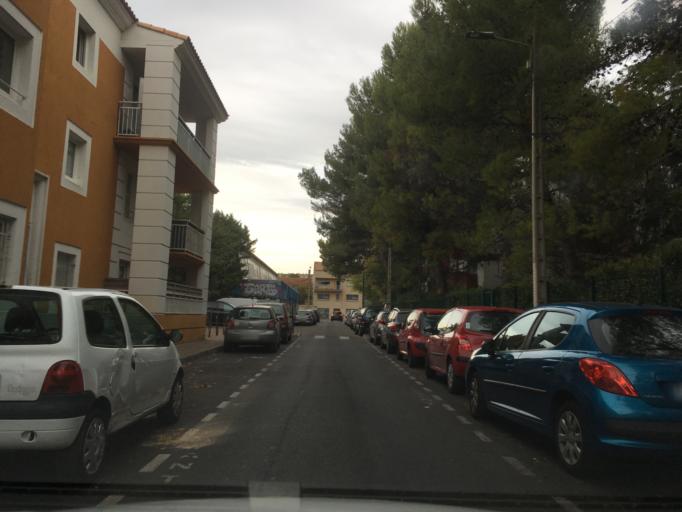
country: FR
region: Languedoc-Roussillon
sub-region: Departement de l'Herault
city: Montpellier
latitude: 43.6177
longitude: 3.8835
